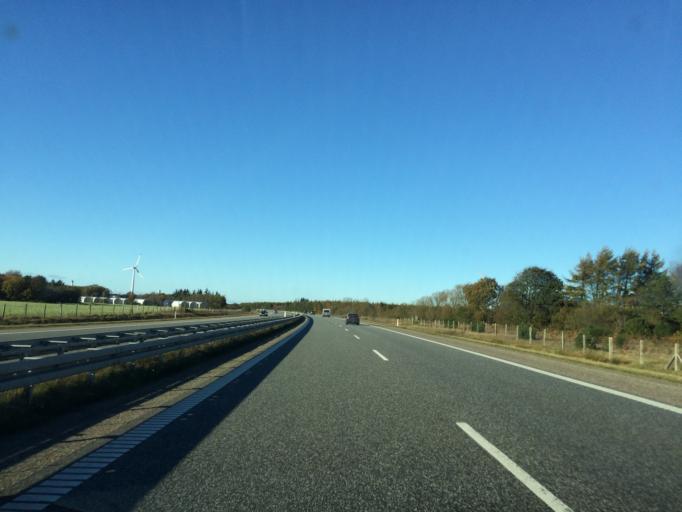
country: DK
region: South Denmark
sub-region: Vejle Kommune
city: Give
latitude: 55.9001
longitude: 9.2117
